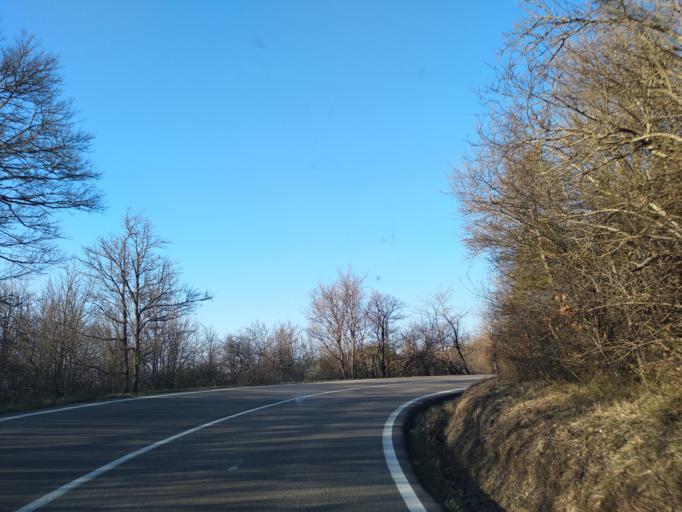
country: IT
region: Emilia-Romagna
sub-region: Provincia di Reggio Emilia
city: Busana
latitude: 44.4072
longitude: 10.3231
